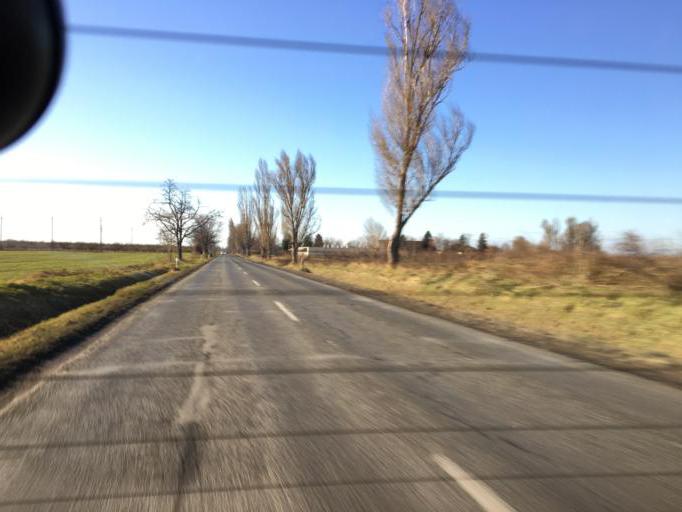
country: HU
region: Pest
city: Kiskunlachaza
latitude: 47.1726
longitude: 18.9805
